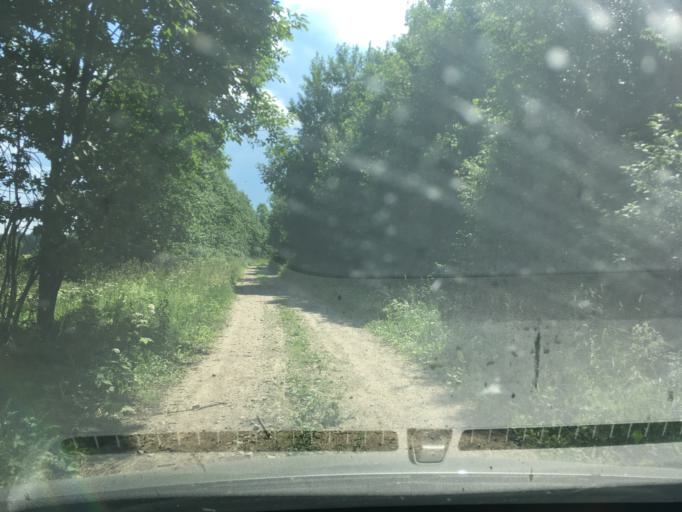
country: EE
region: Raplamaa
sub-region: Maerjamaa vald
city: Marjamaa
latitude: 58.8009
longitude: 24.4598
